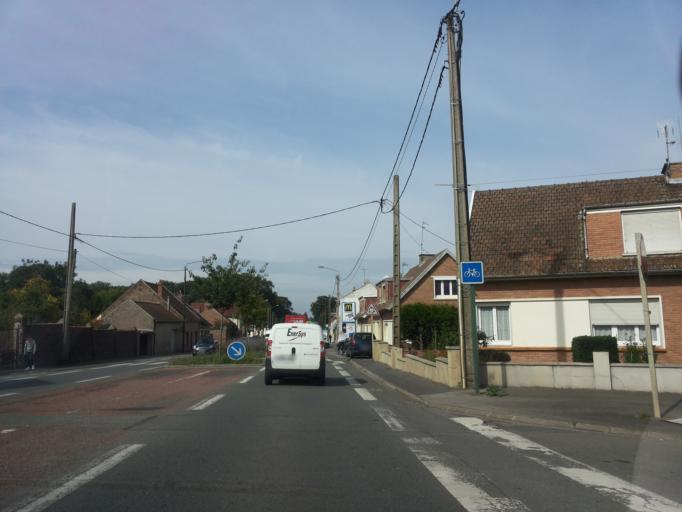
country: FR
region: Nord-Pas-de-Calais
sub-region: Departement du Pas-de-Calais
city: Tilloy-les-Mofflaines
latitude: 50.2793
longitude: 2.8178
